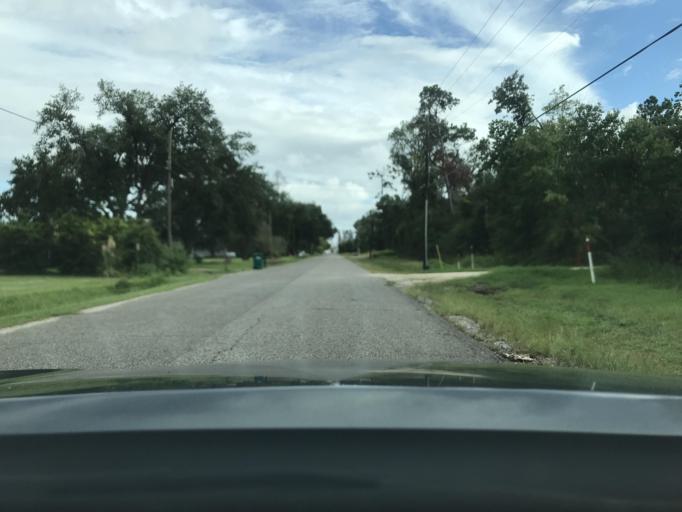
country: US
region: Louisiana
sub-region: Calcasieu Parish
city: Westlake
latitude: 30.2610
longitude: -93.2751
